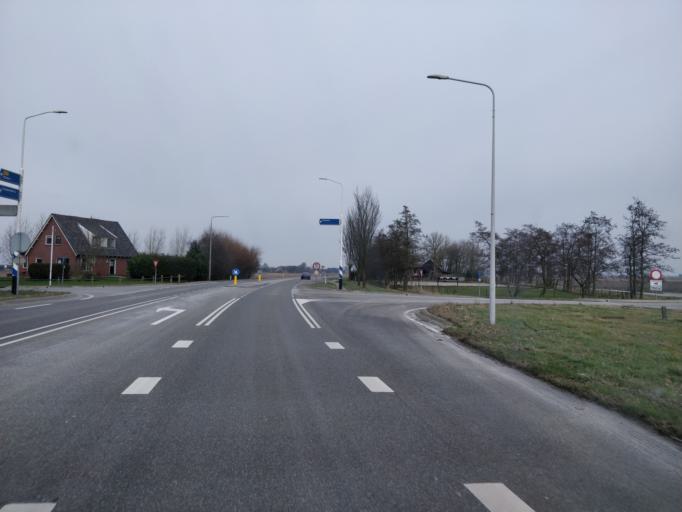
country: NL
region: Friesland
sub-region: Gemeente Leeuwarderadeel
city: Stiens
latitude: 53.2771
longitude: 5.7615
